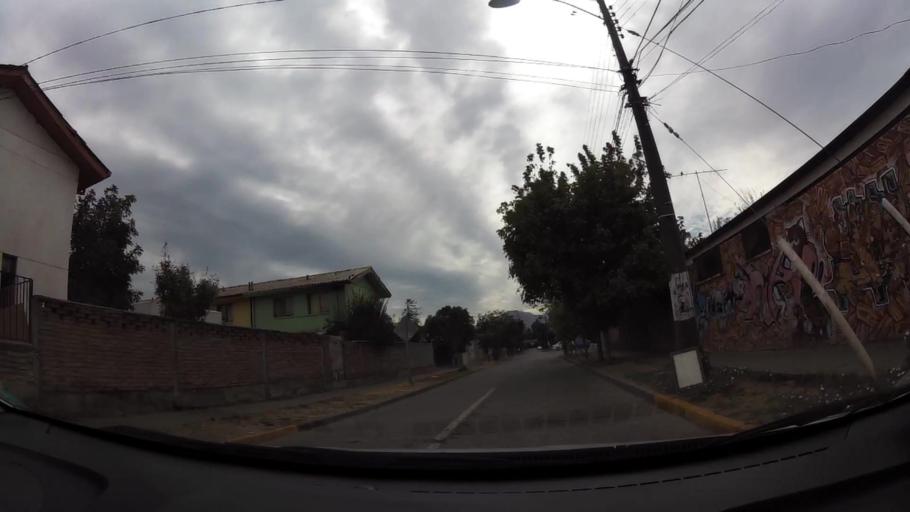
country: CL
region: O'Higgins
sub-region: Provincia de Cachapoal
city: Rancagua
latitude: -34.1585
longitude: -70.7388
